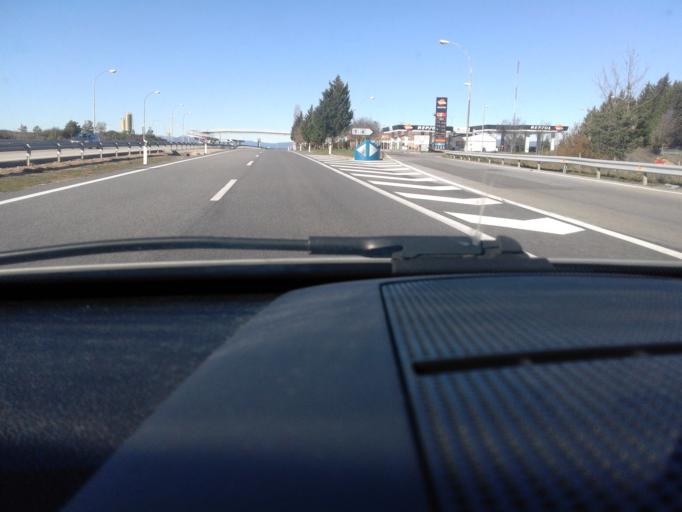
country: ES
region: Castille and Leon
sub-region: Provincia de Leon
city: Santa Maria de Ordas
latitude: 42.6898
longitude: -5.7660
